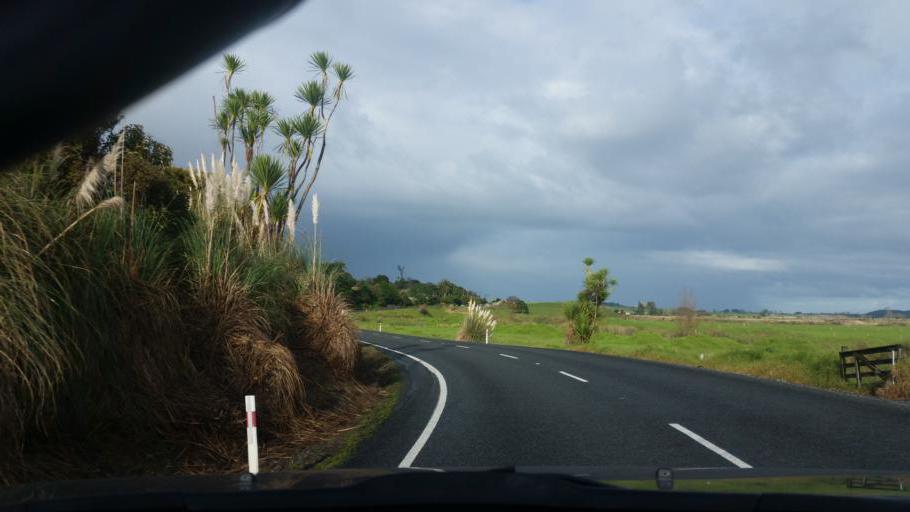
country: NZ
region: Northland
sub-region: Kaipara District
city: Dargaville
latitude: -35.8601
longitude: 173.9369
